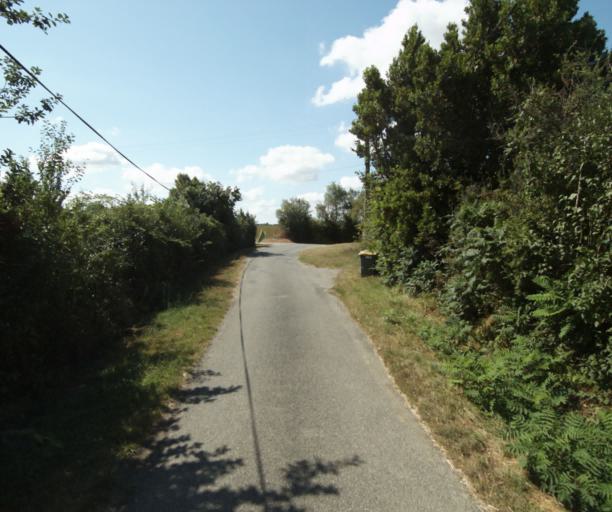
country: FR
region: Midi-Pyrenees
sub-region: Departement de la Haute-Garonne
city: Auriac-sur-Vendinelle
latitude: 43.4603
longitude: 1.7881
